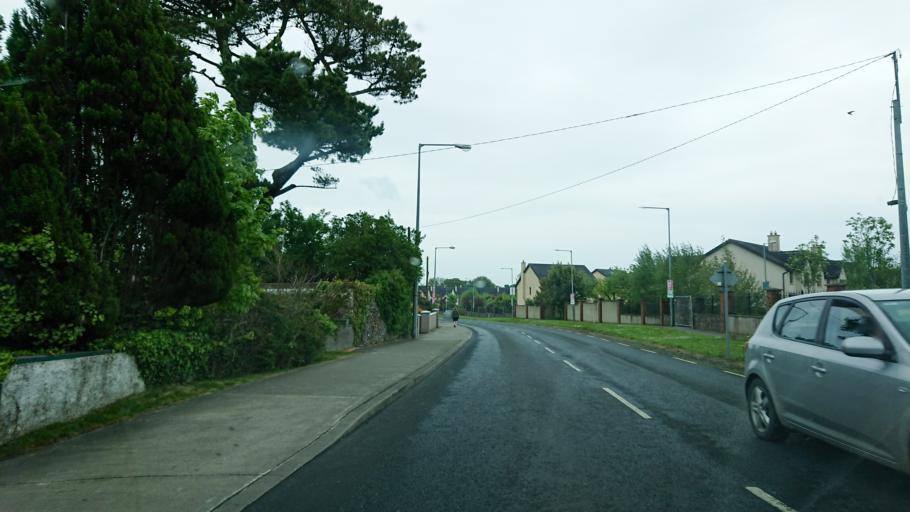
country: IE
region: Munster
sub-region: Waterford
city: Waterford
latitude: 52.2356
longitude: -7.0785
